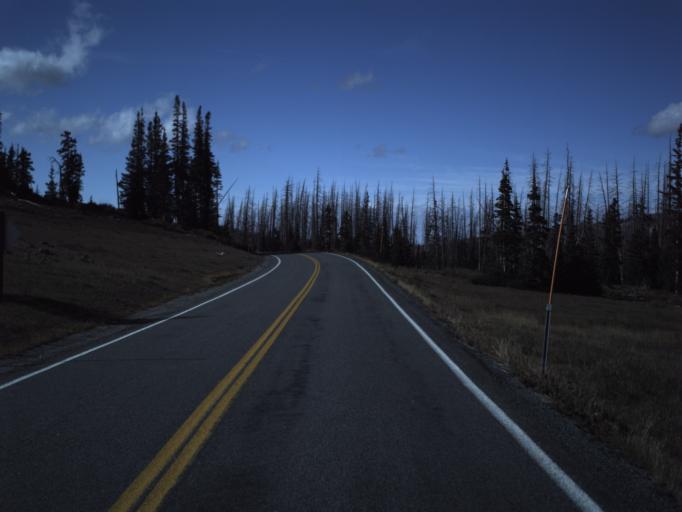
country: US
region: Utah
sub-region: Iron County
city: Parowan
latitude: 37.6551
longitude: -112.8269
